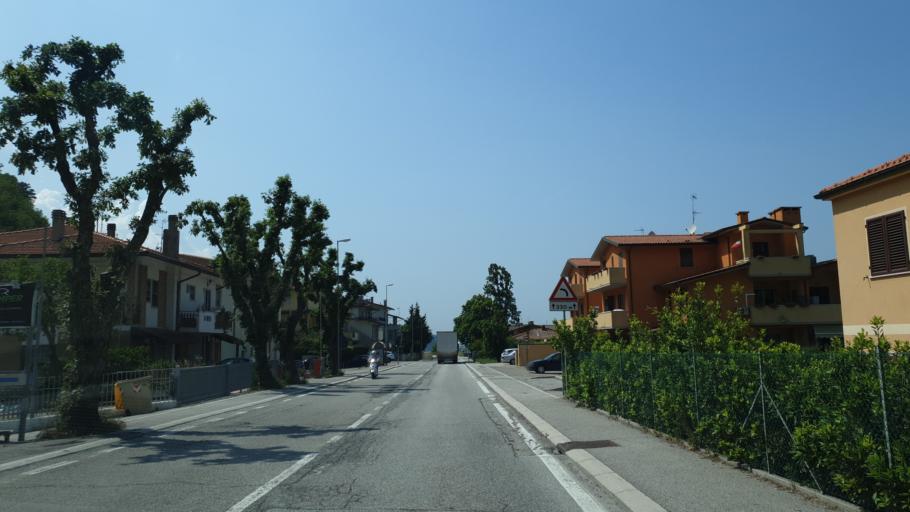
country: SM
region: Acquaviva
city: Acquaviva
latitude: 43.9459
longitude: 12.4284
